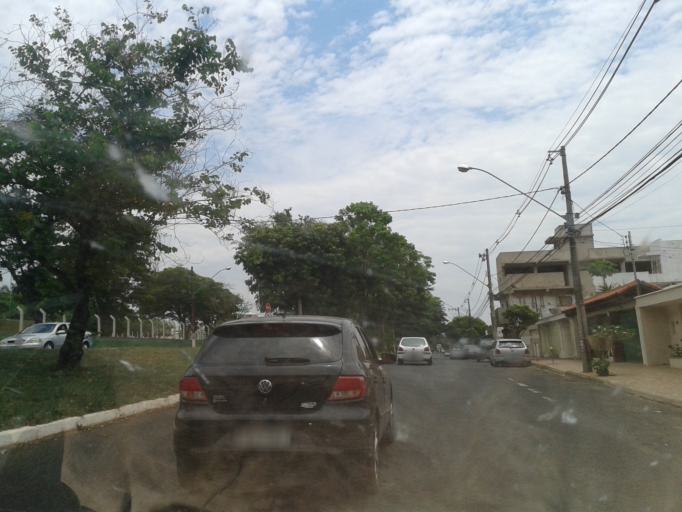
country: BR
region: Minas Gerais
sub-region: Uberlandia
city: Uberlandia
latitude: -18.9231
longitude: -48.3064
